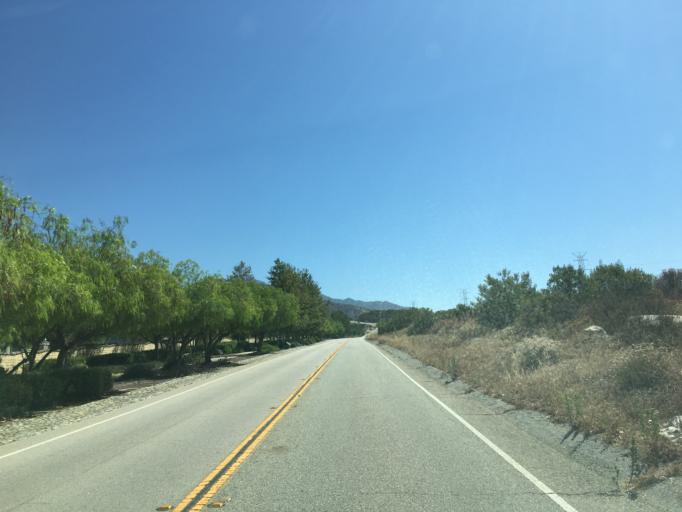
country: US
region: California
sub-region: San Bernardino County
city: San Antonio Heights
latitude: 34.1497
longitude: -117.6943
